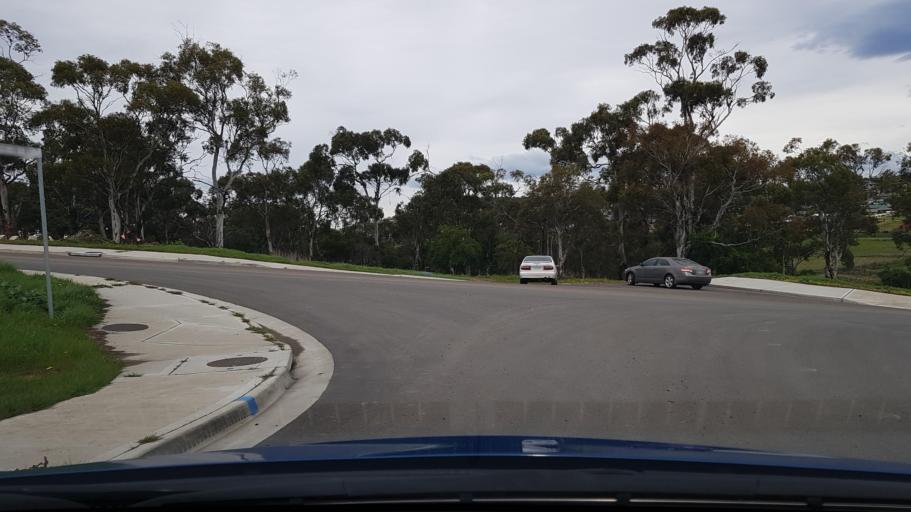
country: AU
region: Tasmania
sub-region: Clarence
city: Rokeby
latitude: -42.8802
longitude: 147.4314
